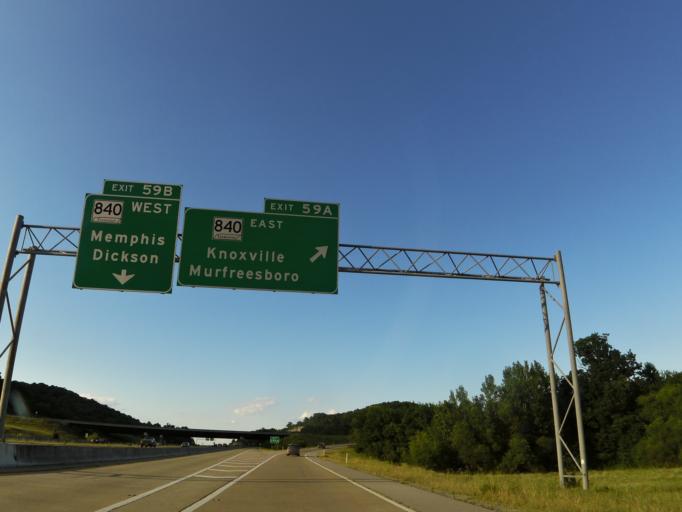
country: US
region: Tennessee
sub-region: Williamson County
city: Thompson's Station
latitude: 35.8193
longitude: -86.8400
